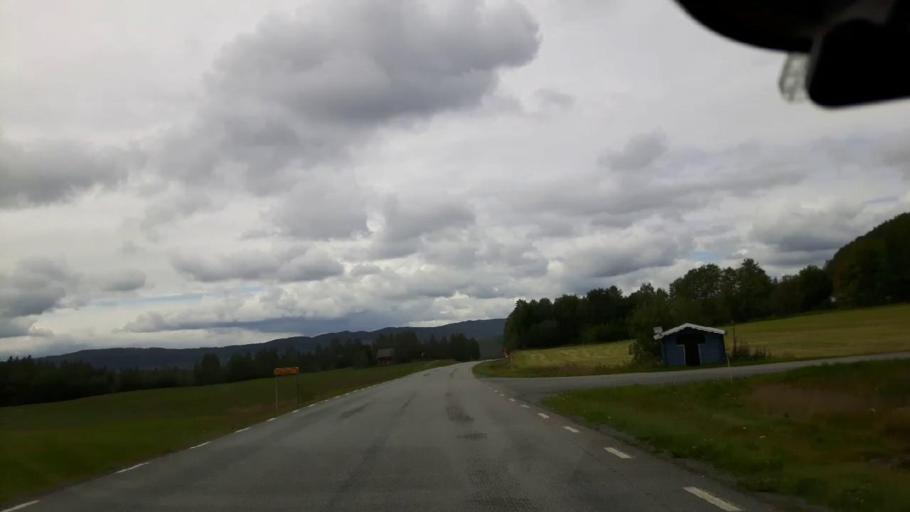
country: SE
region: Jaemtland
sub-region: Krokoms Kommun
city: Krokom
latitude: 63.4537
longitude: 14.1380
